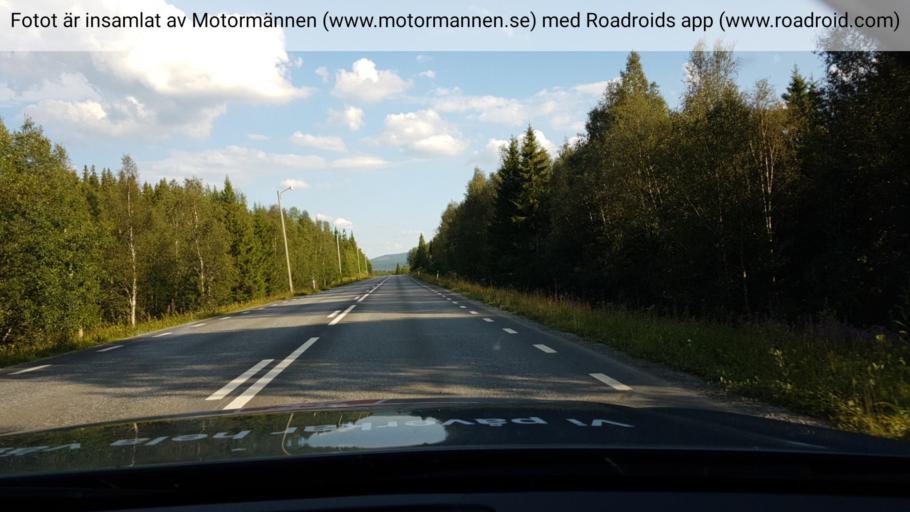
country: SE
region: Jaemtland
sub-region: Are Kommun
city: Are
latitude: 63.3368
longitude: 13.2116
